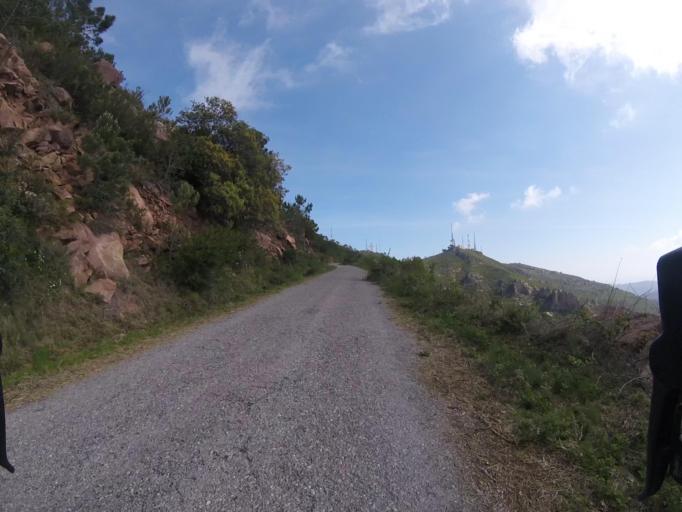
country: ES
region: Valencia
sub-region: Provincia de Castello
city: Benicassim
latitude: 40.0809
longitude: 0.0244
